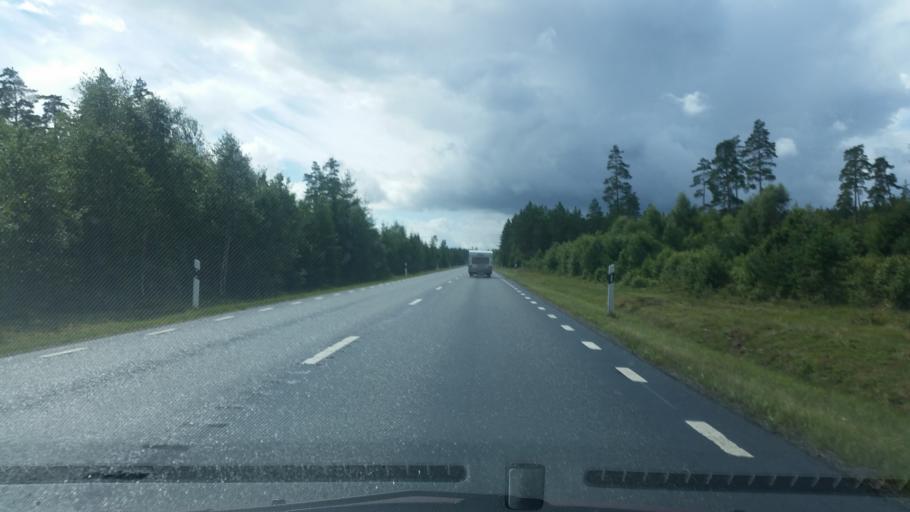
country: SE
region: Joenkoeping
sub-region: Gislaveds Kommun
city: Gislaved
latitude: 57.3701
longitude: 13.5741
